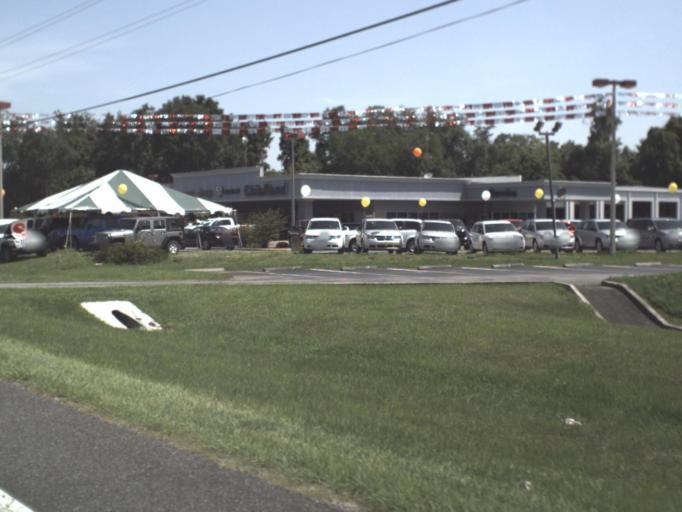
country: US
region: Florida
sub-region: Levy County
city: Manatee Road
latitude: 29.5135
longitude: -82.8772
